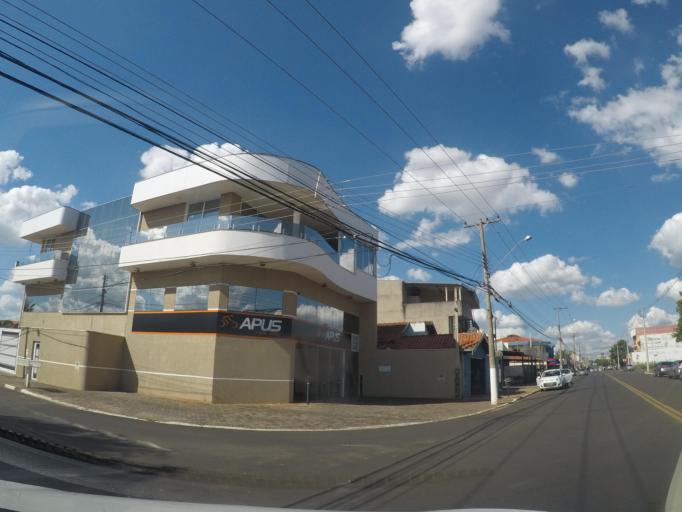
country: BR
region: Sao Paulo
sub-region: Sumare
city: Sumare
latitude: -22.8308
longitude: -47.2783
